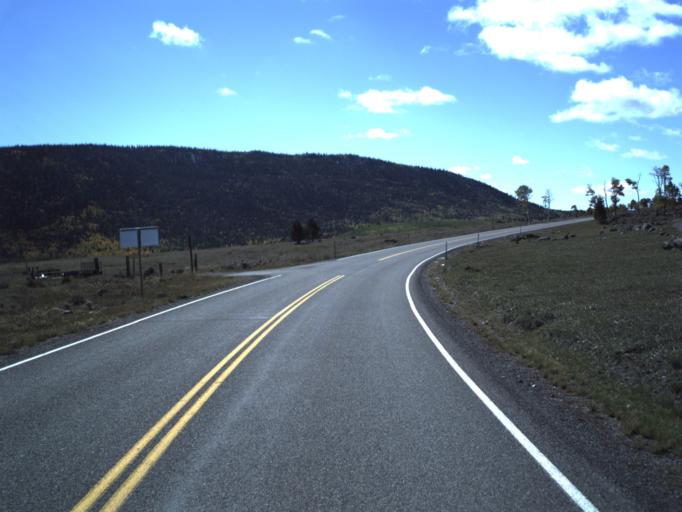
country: US
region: Utah
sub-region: Wayne County
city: Loa
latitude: 38.5349
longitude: -111.7379
